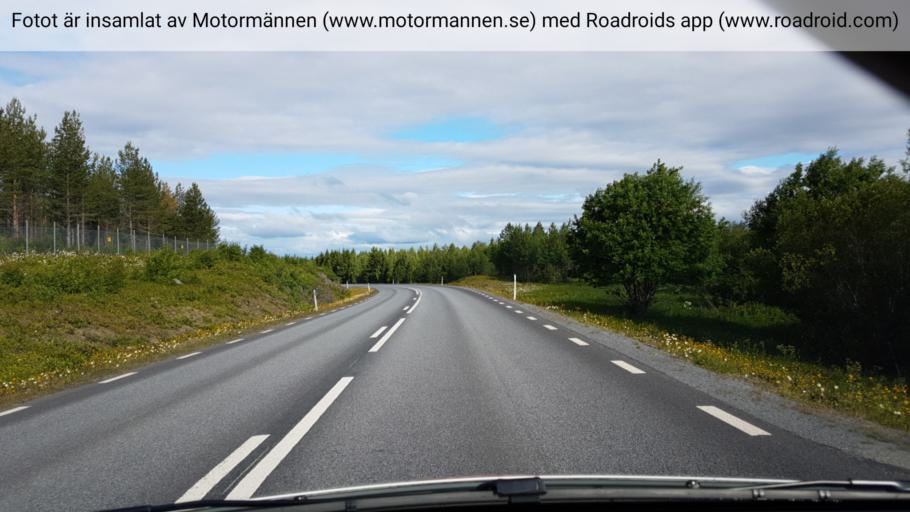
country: SE
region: Jaemtland
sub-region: OEstersunds Kommun
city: Ostersund
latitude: 63.1919
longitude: 14.5281
